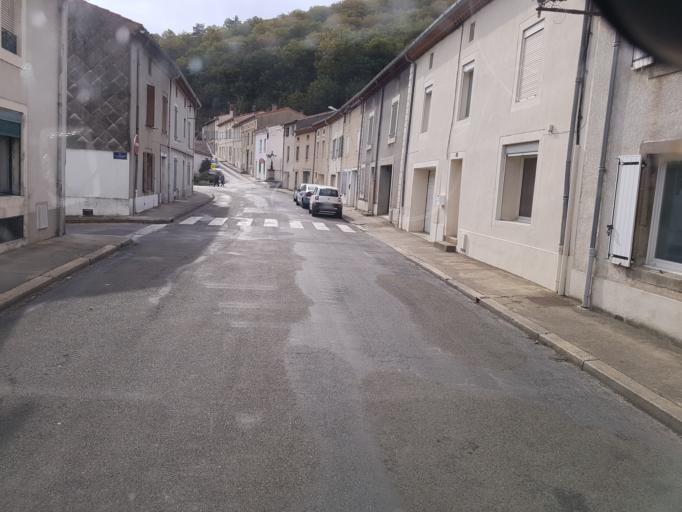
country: FR
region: Midi-Pyrenees
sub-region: Departement du Tarn
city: Mazamet
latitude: 43.4840
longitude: 2.3735
